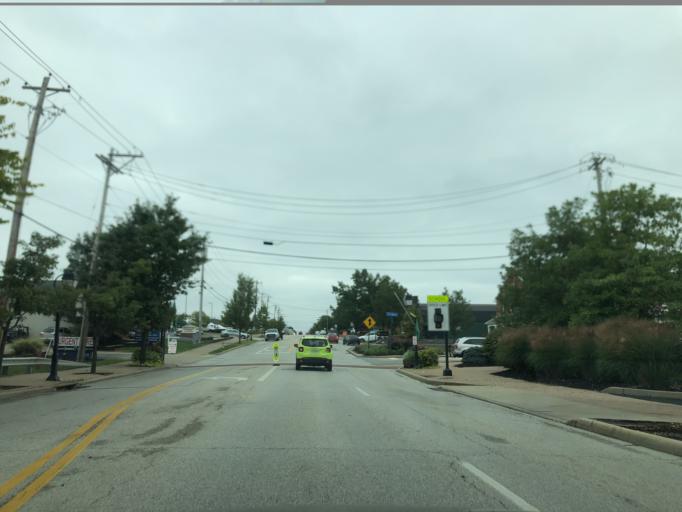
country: US
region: Ohio
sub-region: Hamilton County
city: Montgomery
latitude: 39.2291
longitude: -84.3536
